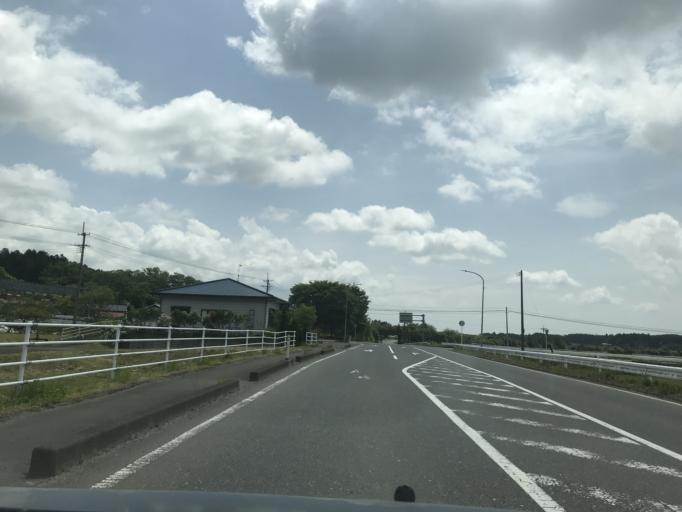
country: JP
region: Miyagi
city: Furukawa
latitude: 38.6792
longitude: 140.9800
